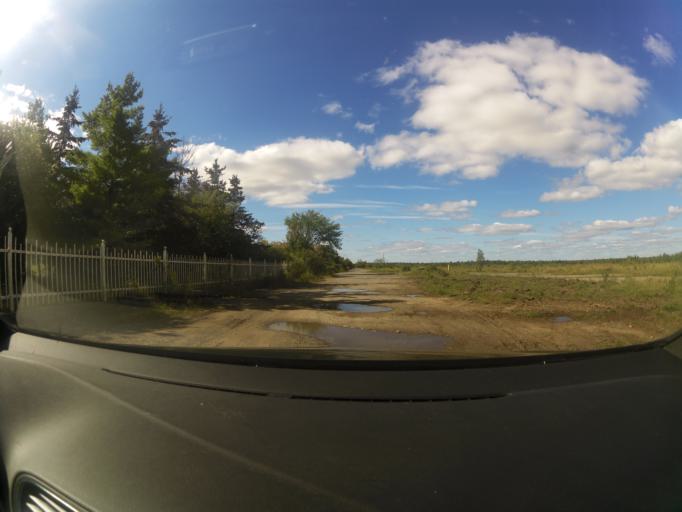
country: CA
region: Ontario
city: Carleton Place
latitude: 45.2551
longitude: -76.1533
